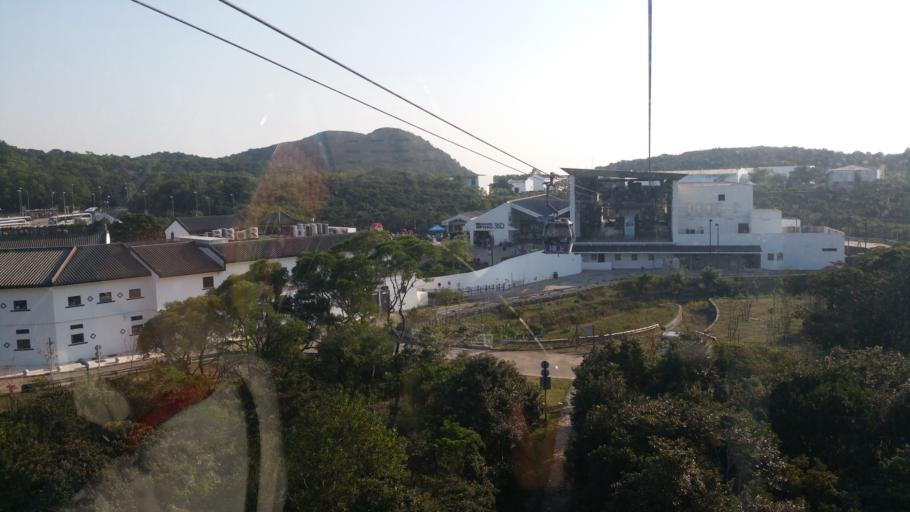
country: HK
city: Tai O
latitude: 22.2576
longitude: 113.9020
